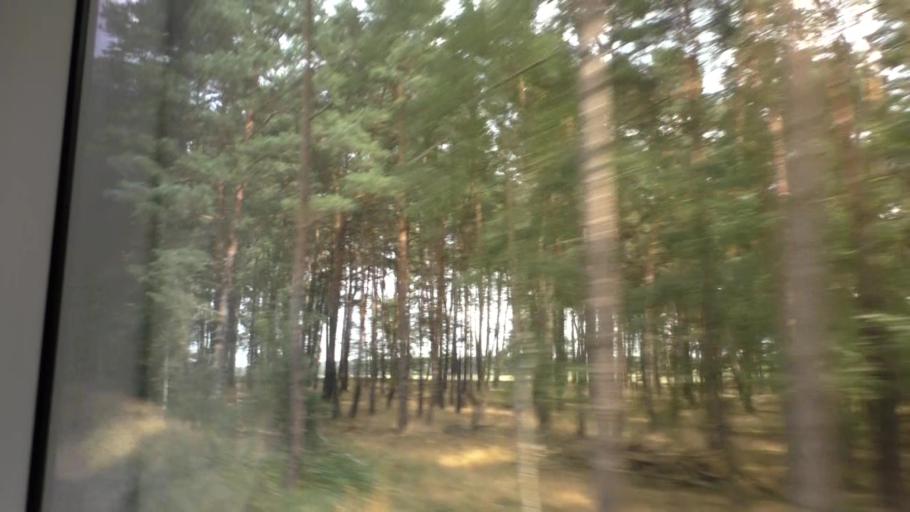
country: DE
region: Brandenburg
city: Mixdorf
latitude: 52.2047
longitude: 14.4021
